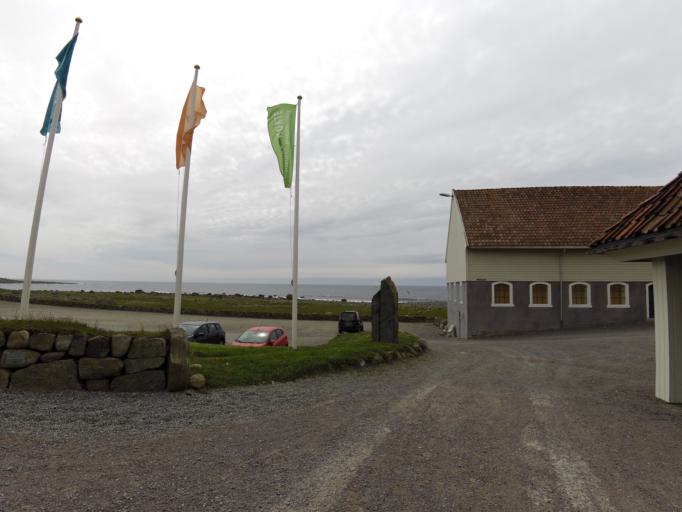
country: NO
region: Rogaland
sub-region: Ha
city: Naerbo
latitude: 58.6670
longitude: 5.5510
